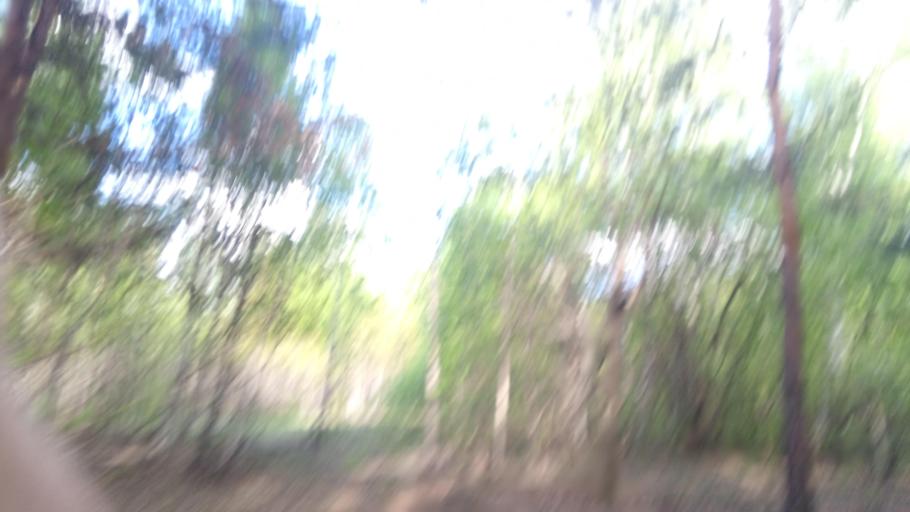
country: RU
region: Chelyabinsk
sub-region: Gorod Chelyabinsk
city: Chelyabinsk
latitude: 55.1677
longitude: 61.3300
